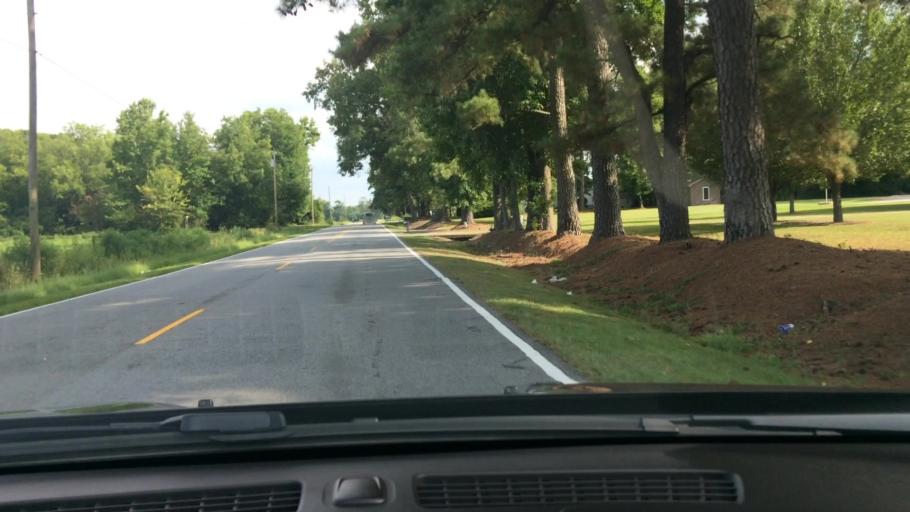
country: US
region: North Carolina
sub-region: Pitt County
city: Winterville
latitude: 35.4980
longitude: -77.3791
